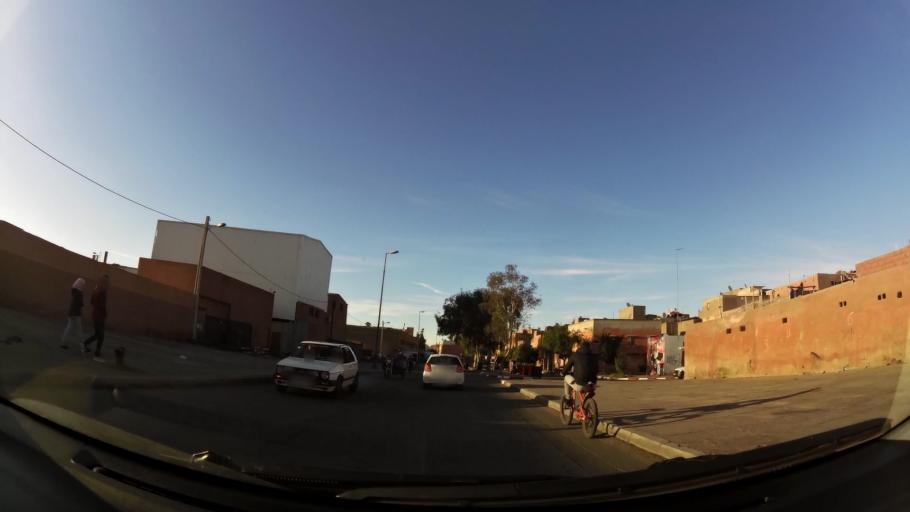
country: MA
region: Marrakech-Tensift-Al Haouz
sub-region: Marrakech
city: Marrakesh
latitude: 31.6249
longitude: -8.0432
